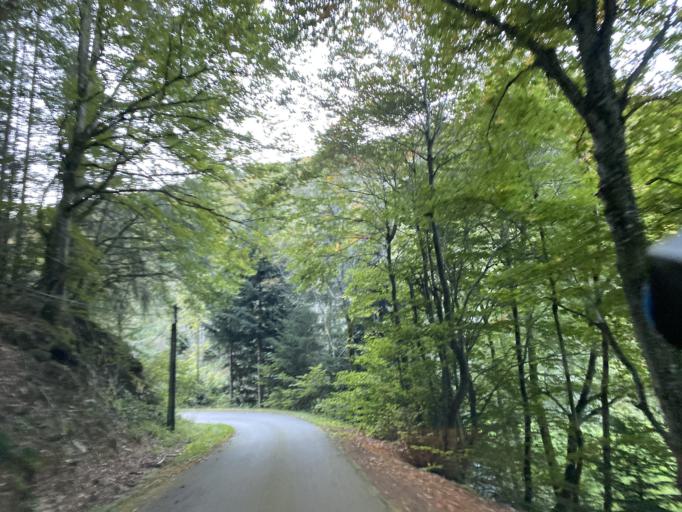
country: FR
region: Rhone-Alpes
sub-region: Departement de la Loire
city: Saint-Just-en-Chevalet
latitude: 45.9482
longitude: 3.8553
